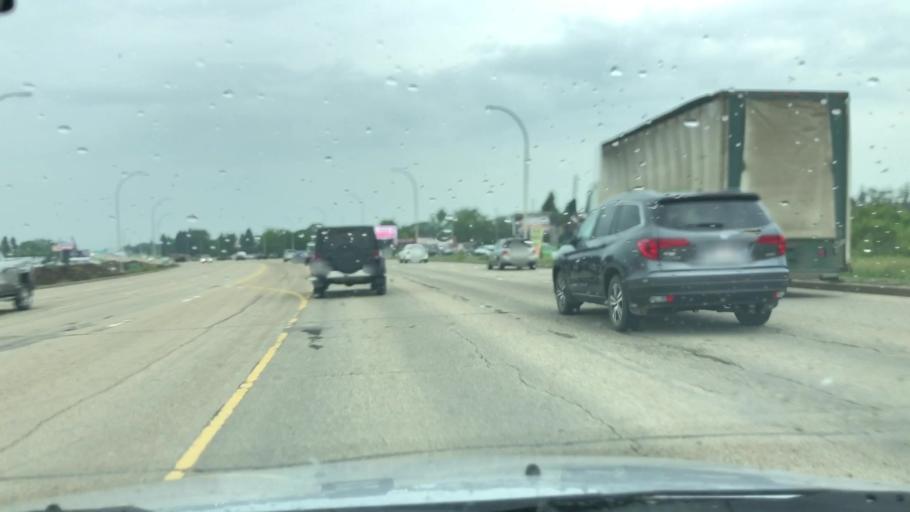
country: CA
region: Alberta
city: St. Albert
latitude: 53.6057
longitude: -113.5799
